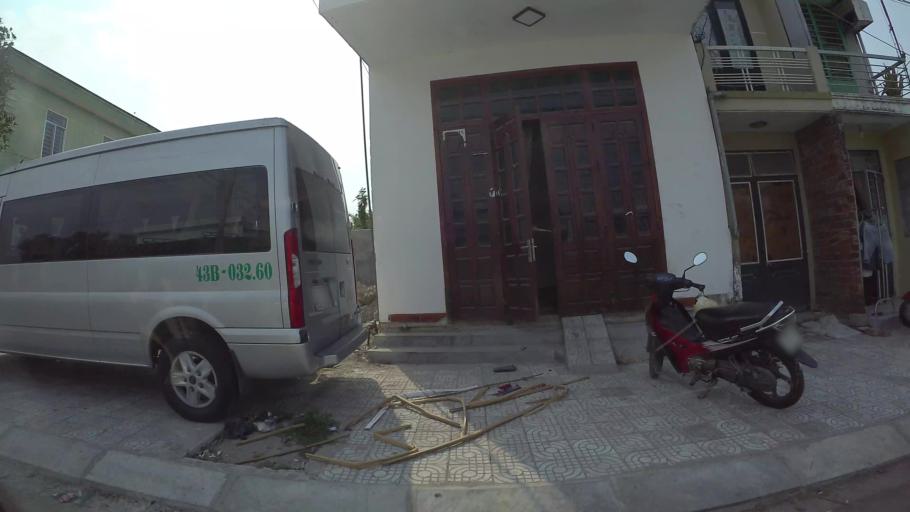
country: VN
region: Da Nang
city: Lien Chieu
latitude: 16.0547
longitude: 108.1563
